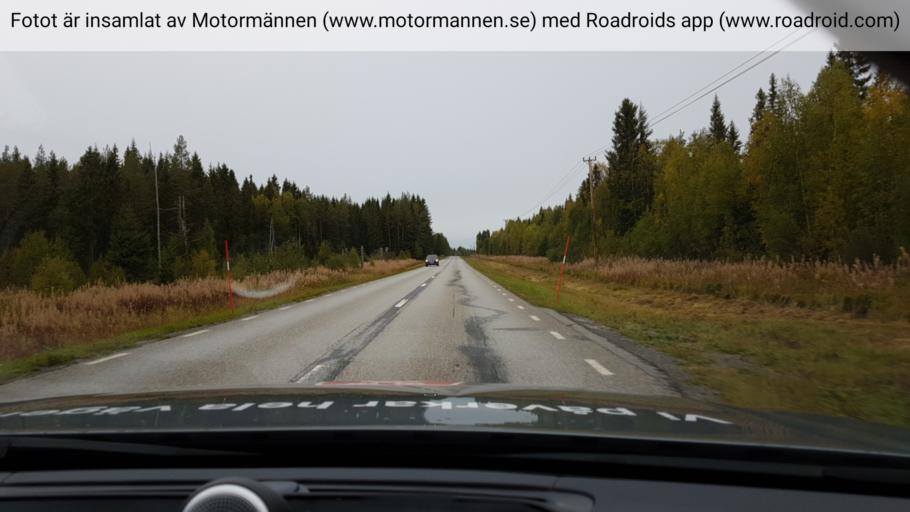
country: SE
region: Jaemtland
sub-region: Stroemsunds Kommun
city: Stroemsund
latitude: 63.9274
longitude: 15.5063
